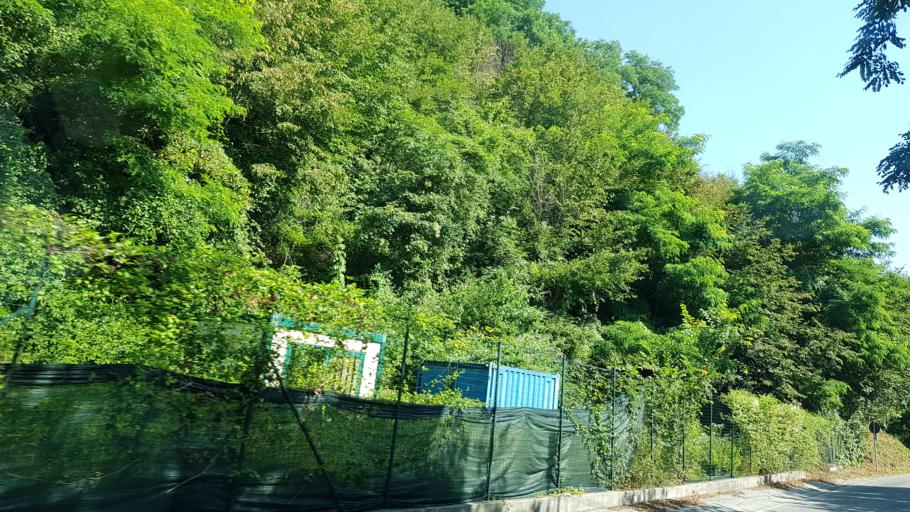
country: IT
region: Liguria
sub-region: Provincia di Genova
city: Serra Ricco
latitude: 44.5193
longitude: 8.9394
